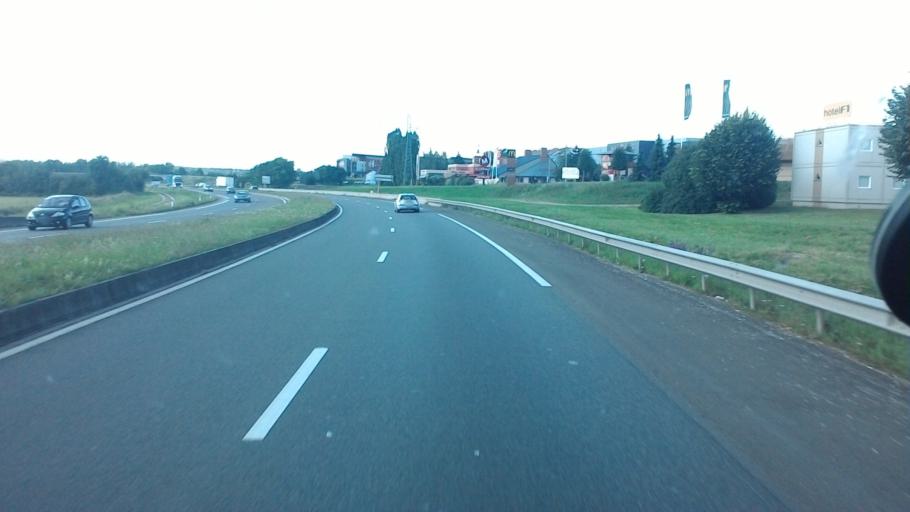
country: FR
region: Franche-Comte
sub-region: Departement de la Haute-Saone
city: Noidans-les-Vesoul
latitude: 47.6305
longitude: 6.1385
